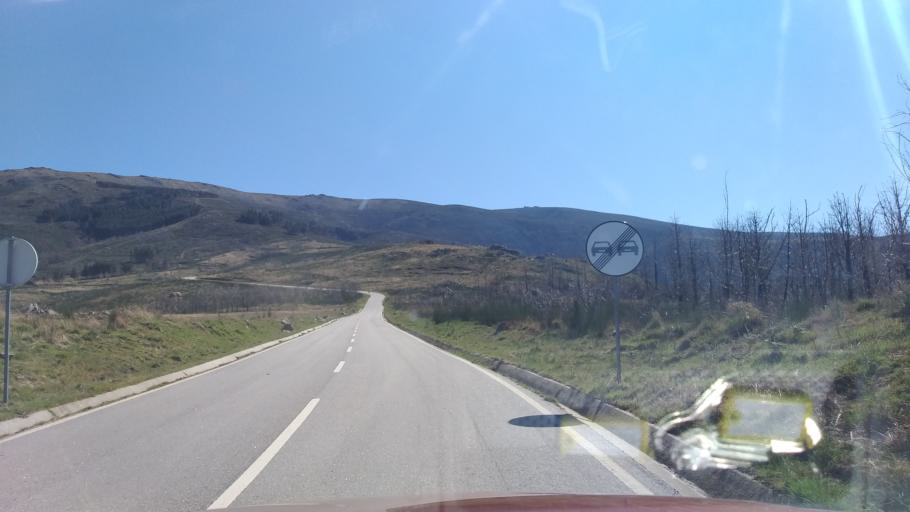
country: PT
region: Guarda
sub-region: Manteigas
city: Manteigas
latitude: 40.4908
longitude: -7.5676
